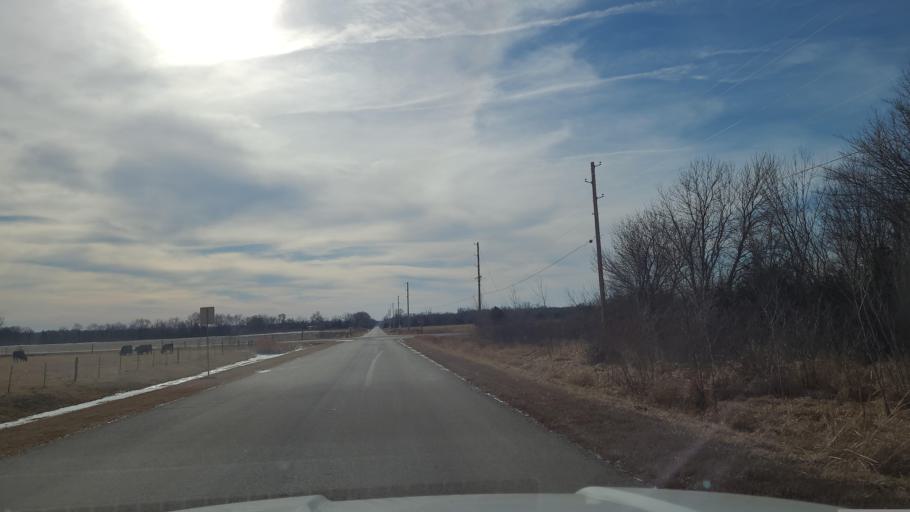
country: US
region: Kansas
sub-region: Douglas County
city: Lawrence
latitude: 38.9002
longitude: -95.2052
